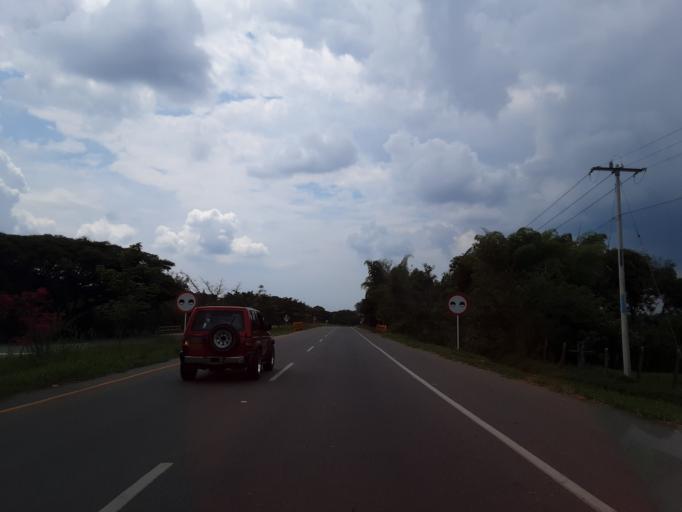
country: CO
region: Cauca
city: Santander de Quilichao
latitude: 3.0257
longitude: -76.4816
